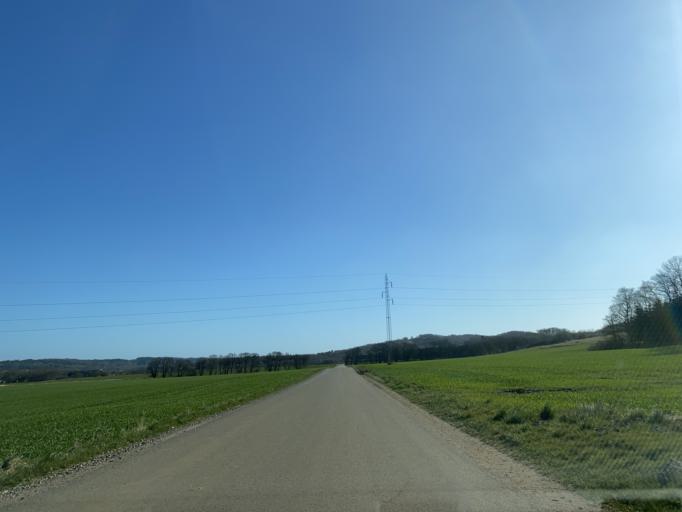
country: DK
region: Central Jutland
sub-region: Viborg Kommune
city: Bjerringbro
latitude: 56.3752
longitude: 9.7191
